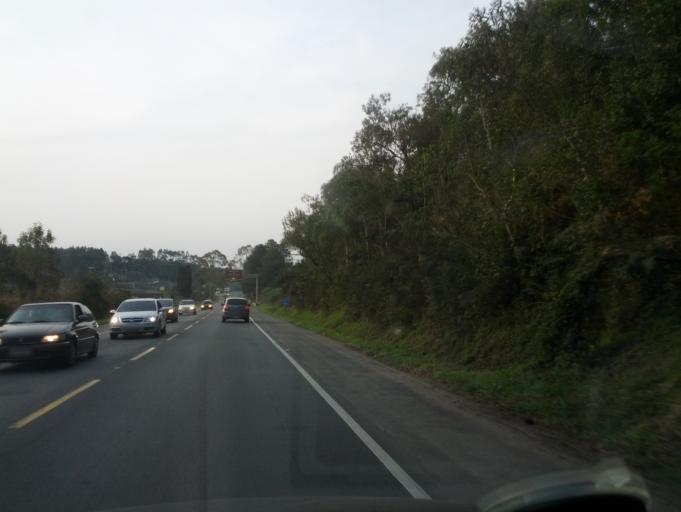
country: BR
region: Santa Catarina
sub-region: Otacilio Costa
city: Otacilio Costa
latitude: -27.2889
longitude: -50.0778
